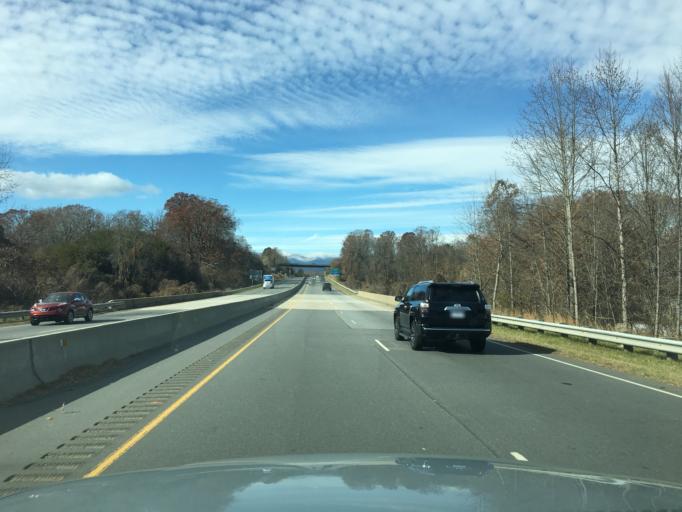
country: US
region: North Carolina
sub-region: McDowell County
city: Marion
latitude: 35.6748
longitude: -82.0179
